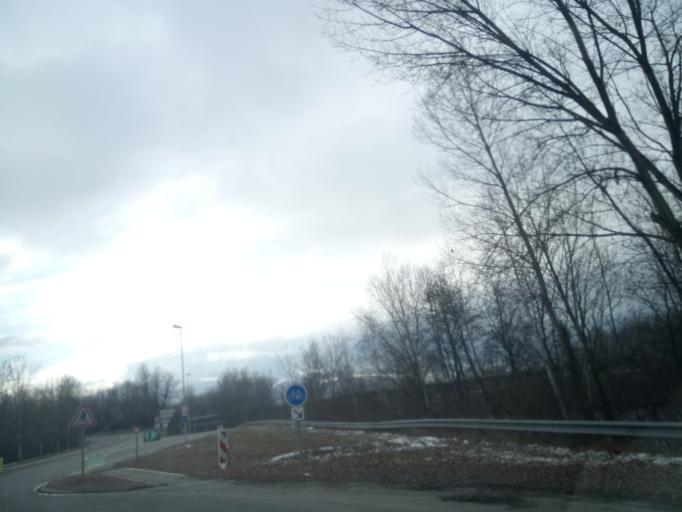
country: FR
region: Rhone-Alpes
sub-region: Departement de la Savoie
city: Montmelian
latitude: 45.4877
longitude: 6.0438
